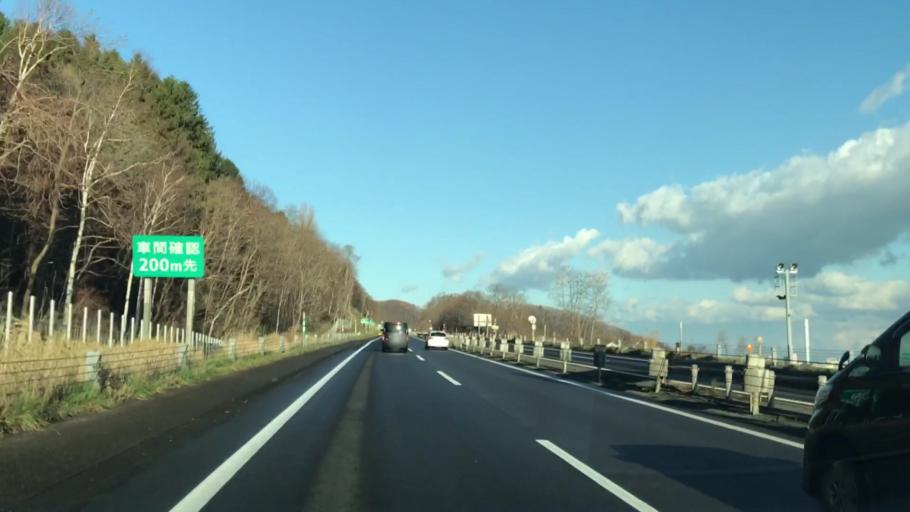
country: JP
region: Hokkaido
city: Sapporo
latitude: 43.0964
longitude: 141.2520
